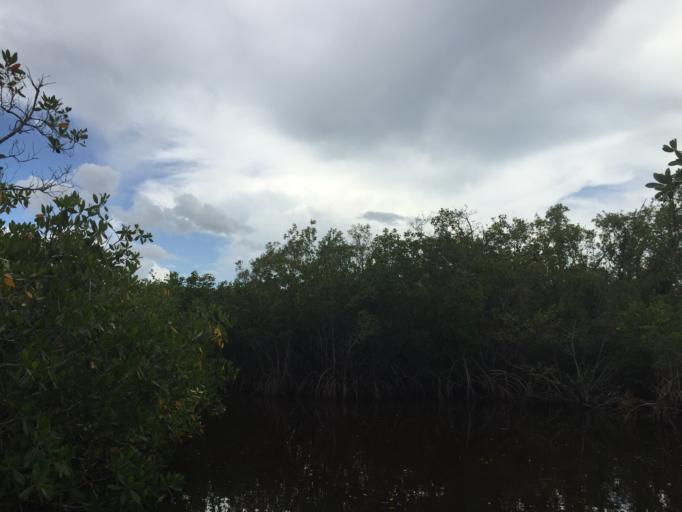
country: US
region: Florida
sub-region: Collier County
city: Marco
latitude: 25.9015
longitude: -81.3747
